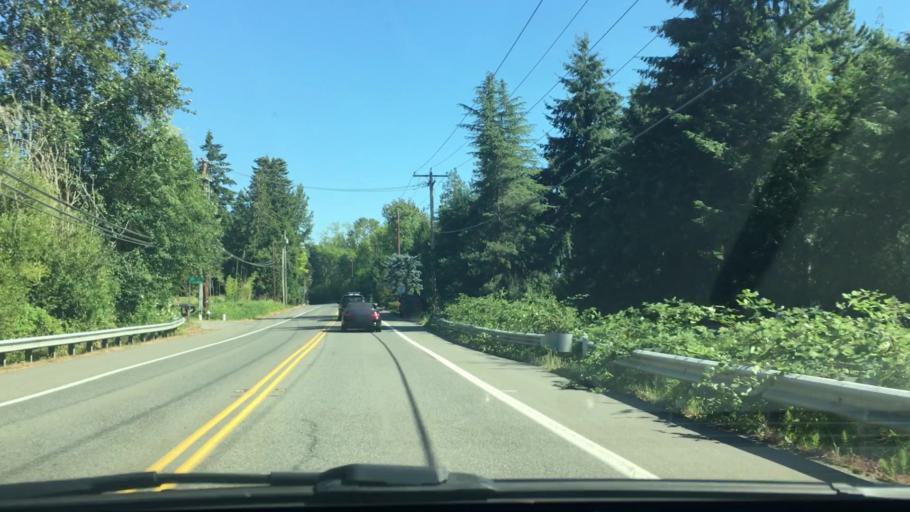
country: US
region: Washington
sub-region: King County
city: Sammamish
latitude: 47.6428
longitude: -122.0817
